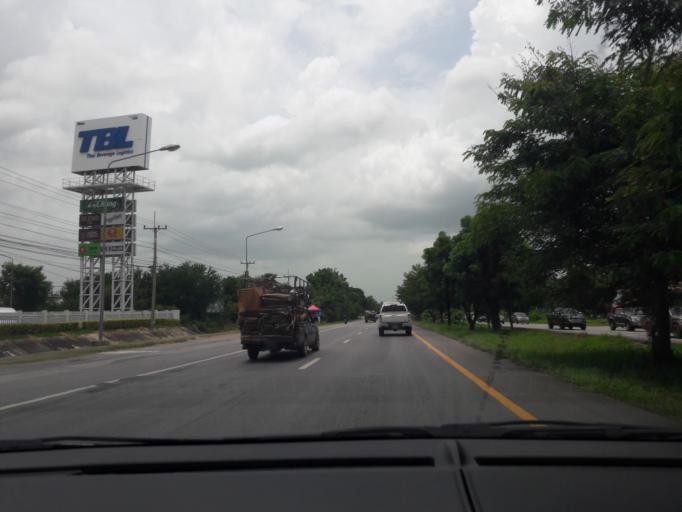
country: TH
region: Nakhon Ratchasima
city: Chaloem Phra Kiat
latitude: 15.0681
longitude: 102.1996
